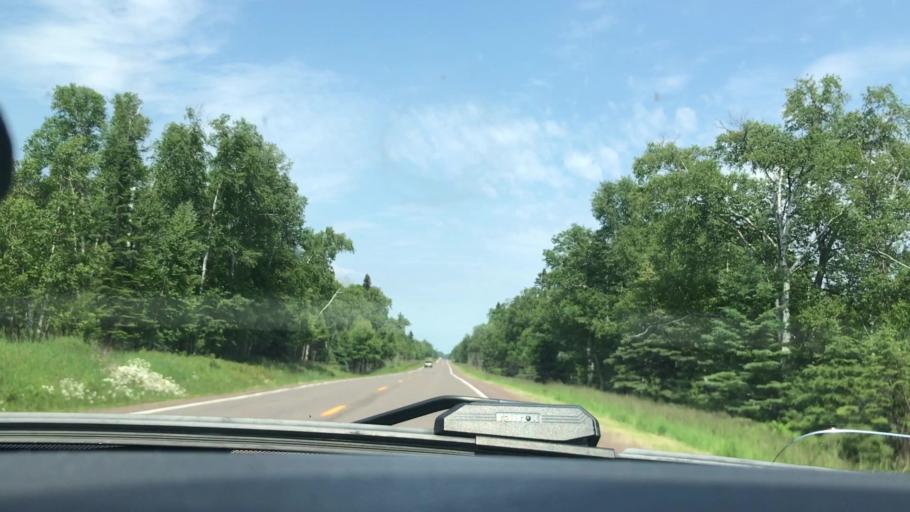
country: US
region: Minnesota
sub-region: Lake County
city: Silver Bay
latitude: 47.5019
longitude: -90.9648
